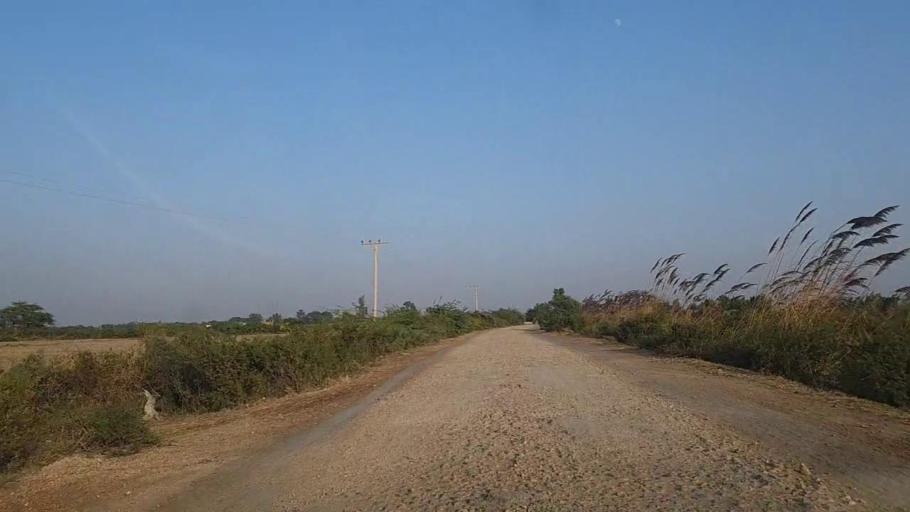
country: PK
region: Sindh
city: Keti Bandar
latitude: 24.2769
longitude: 67.6491
